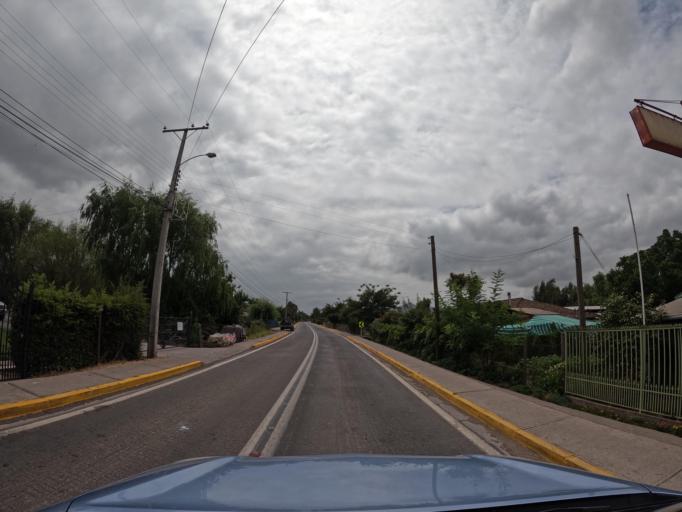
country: CL
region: Maule
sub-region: Provincia de Curico
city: Teno
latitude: -34.7771
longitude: -71.1674
